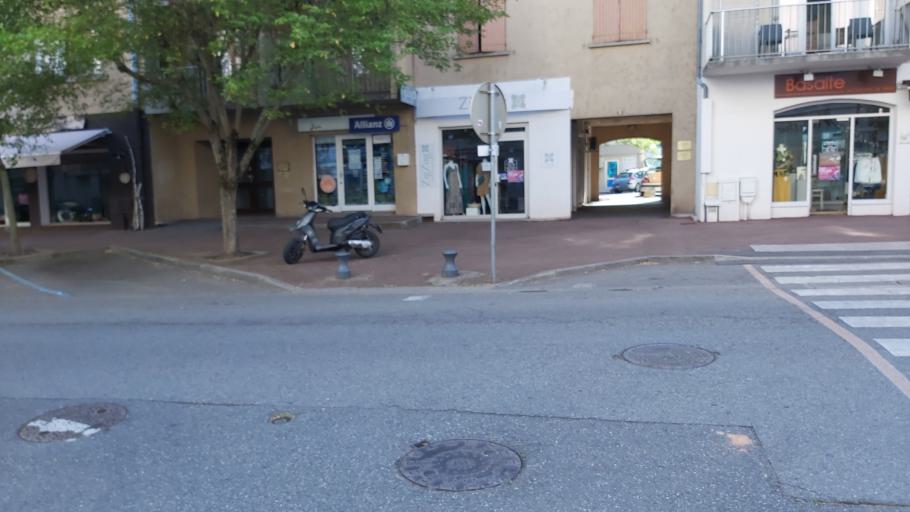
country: FR
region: Rhone-Alpes
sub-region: Departement de l'Ardeche
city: Annonay
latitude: 45.2418
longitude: 4.6725
